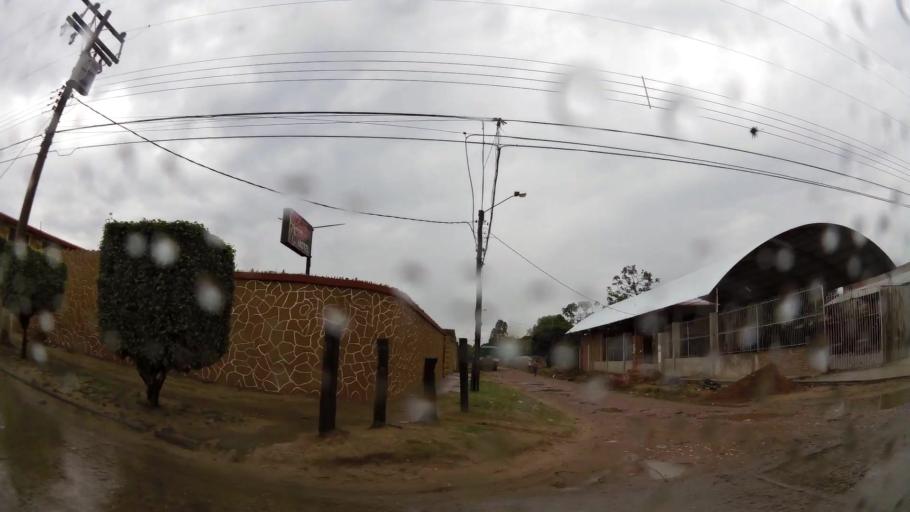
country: BO
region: Santa Cruz
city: Santa Cruz de la Sierra
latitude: -17.8120
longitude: -63.1342
